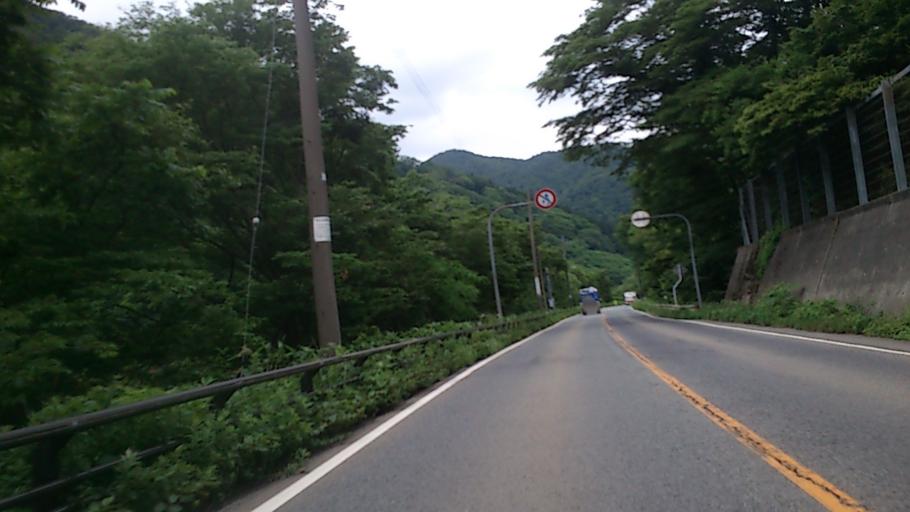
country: JP
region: Yamagata
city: Shinjo
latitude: 38.7561
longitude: 140.0884
